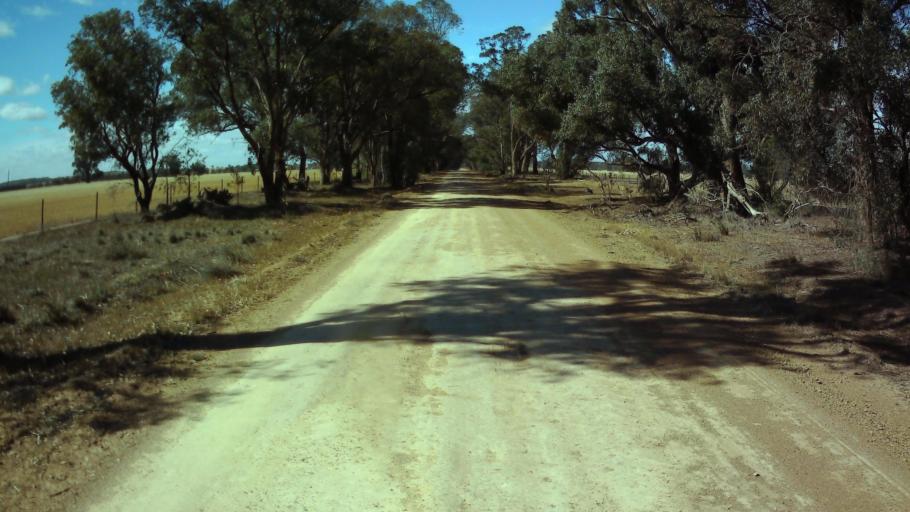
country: AU
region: New South Wales
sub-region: Weddin
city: Grenfell
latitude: -34.0482
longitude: 148.3144
